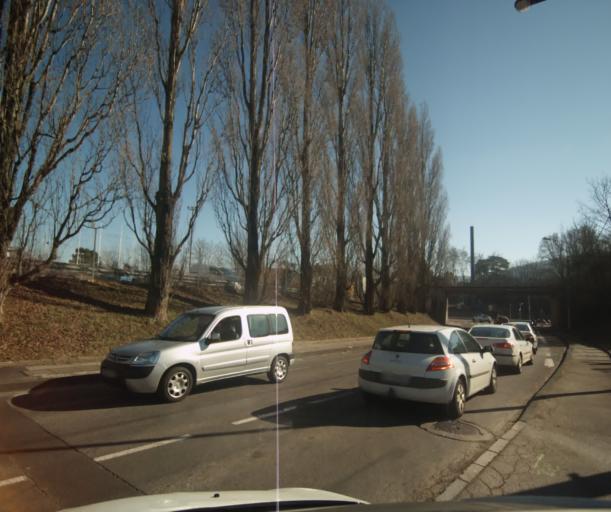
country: FR
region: Franche-Comte
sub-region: Departement du Doubs
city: Pirey
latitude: 47.2349
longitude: 5.9834
